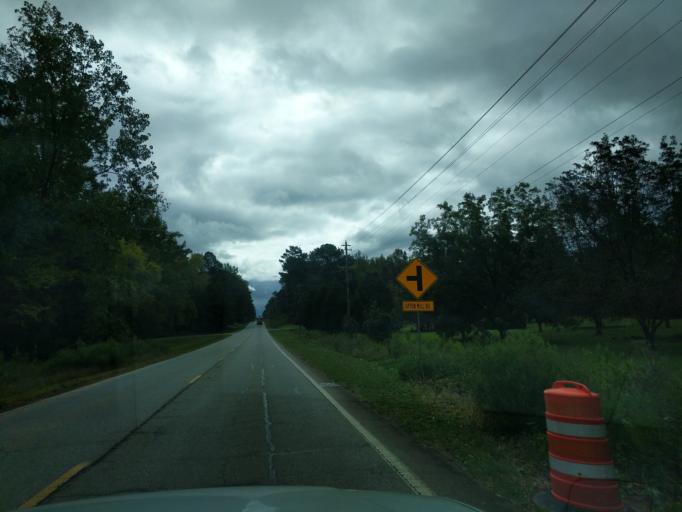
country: US
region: Georgia
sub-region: Wilkes County
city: Washington
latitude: 33.6935
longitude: -82.6781
